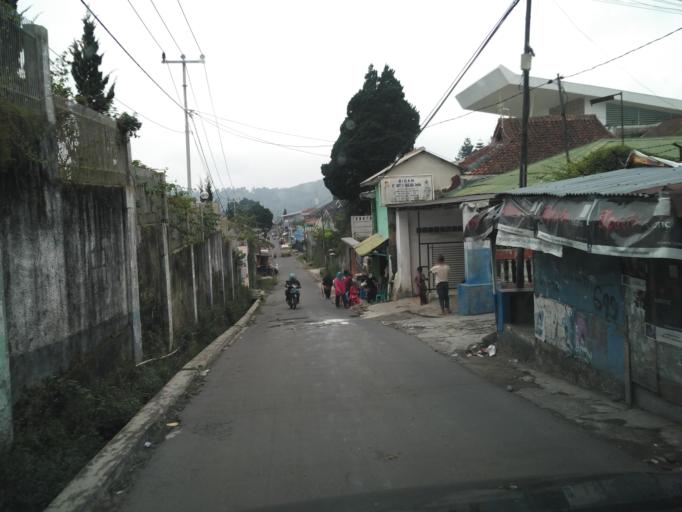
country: ID
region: West Java
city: Sukabumi
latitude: -6.7421
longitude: 107.0429
